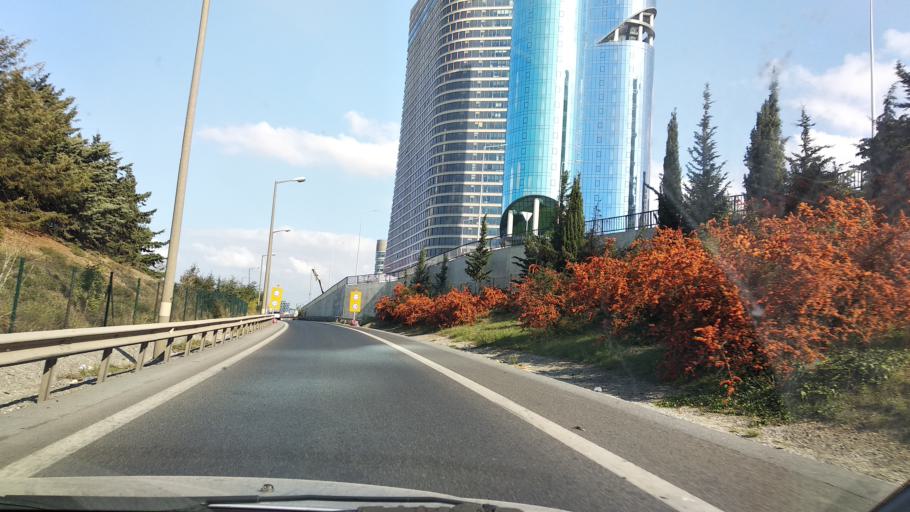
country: TR
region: Istanbul
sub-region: Atasehir
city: Atasehir
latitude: 40.9935
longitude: 29.1161
